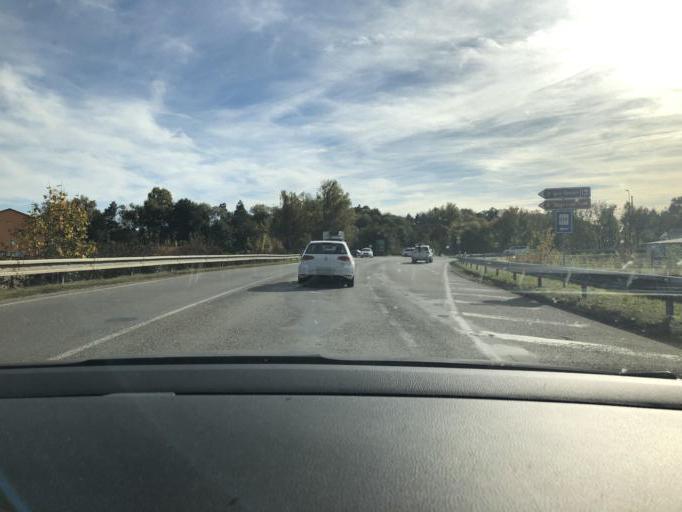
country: CZ
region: Central Bohemia
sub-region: Okres Benesov
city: Benesov
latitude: 49.7828
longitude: 14.7014
